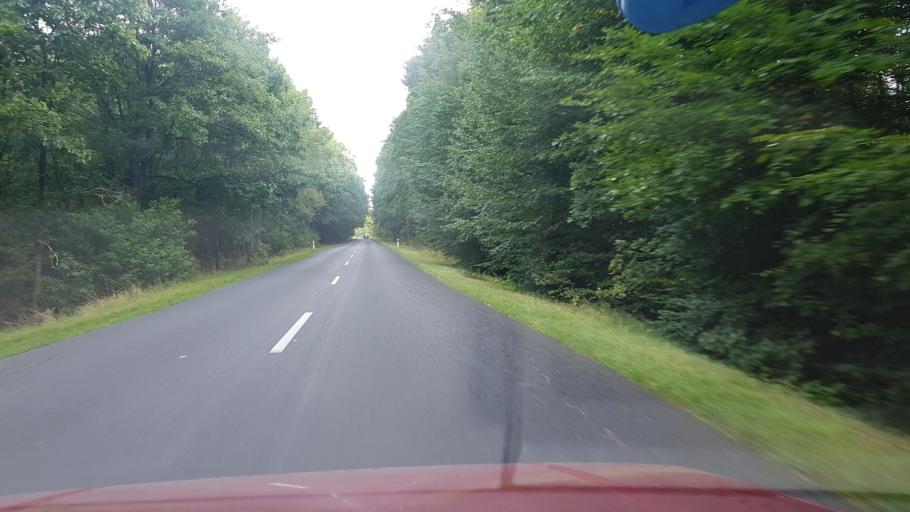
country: PL
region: West Pomeranian Voivodeship
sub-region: Powiat koszalinski
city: Polanow
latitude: 54.1170
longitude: 16.7322
